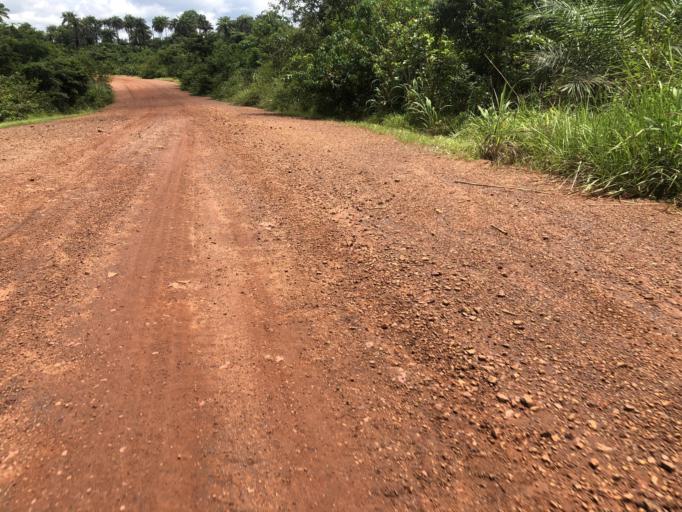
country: SL
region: Northern Province
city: Port Loko
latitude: 8.7140
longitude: -12.8316
